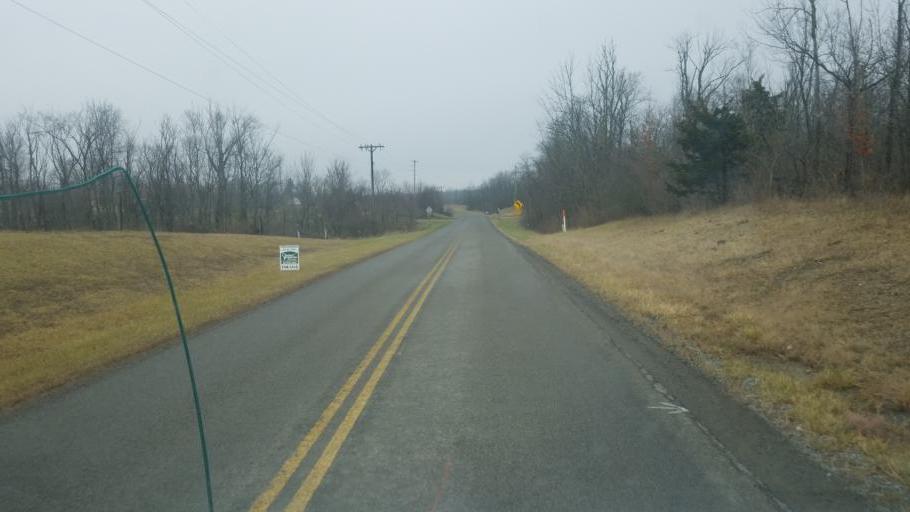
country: US
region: Ohio
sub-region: Champaign County
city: North Lewisburg
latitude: 40.2968
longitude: -83.5780
